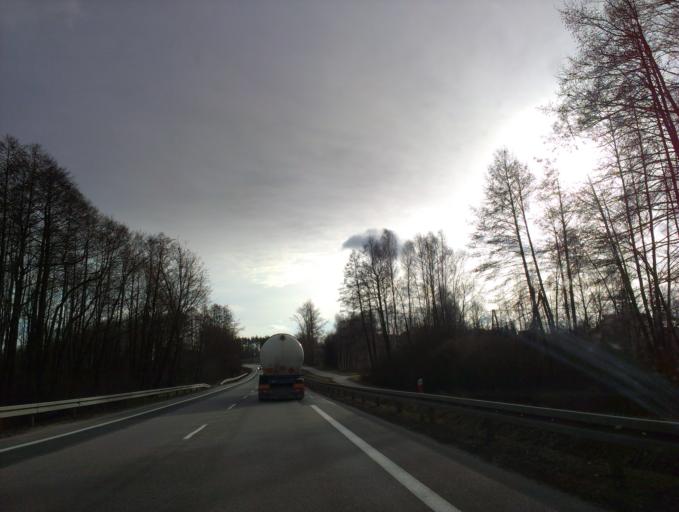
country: PL
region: Kujawsko-Pomorskie
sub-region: Powiat lipnowski
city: Kikol
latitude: 52.8981
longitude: 19.1221
